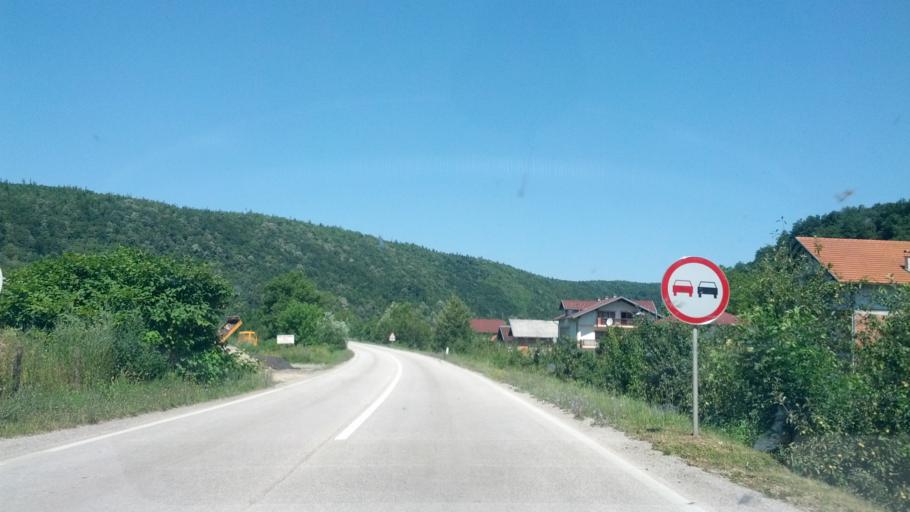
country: BA
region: Federation of Bosnia and Herzegovina
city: Bosanska Krupa
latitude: 44.9135
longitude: 16.1556
